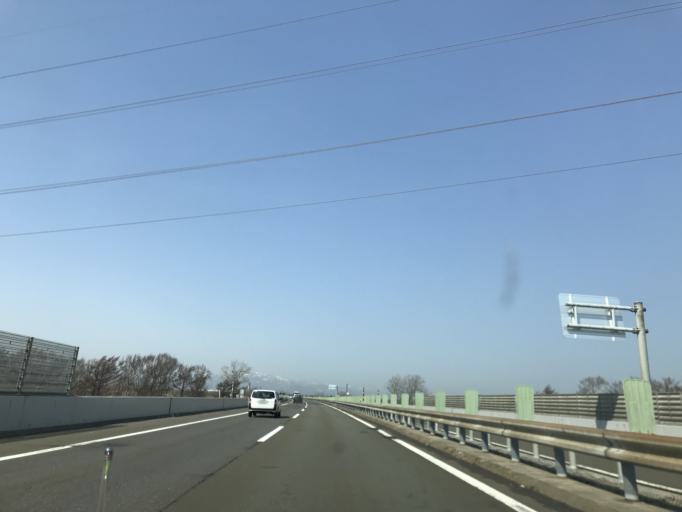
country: JP
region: Hokkaido
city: Ebetsu
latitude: 43.0946
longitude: 141.4859
